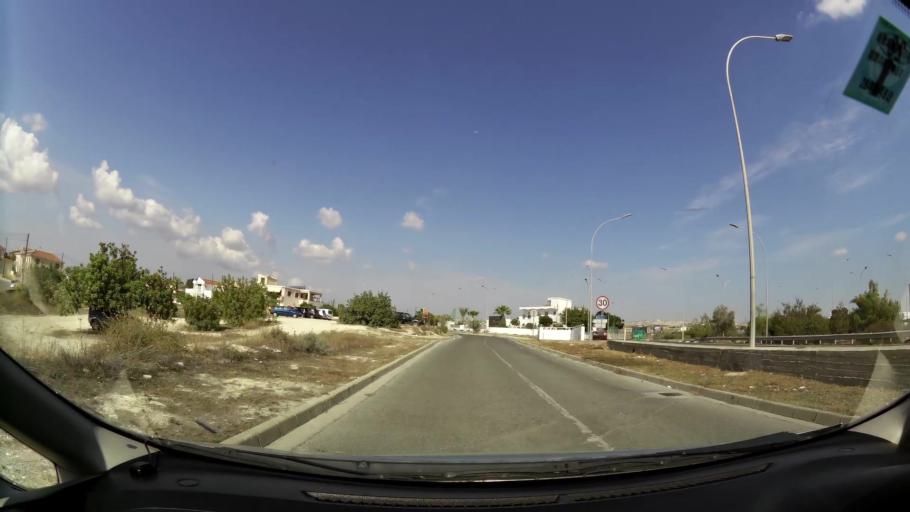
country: CY
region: Larnaka
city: Aradippou
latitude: 34.9490
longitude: 33.5745
